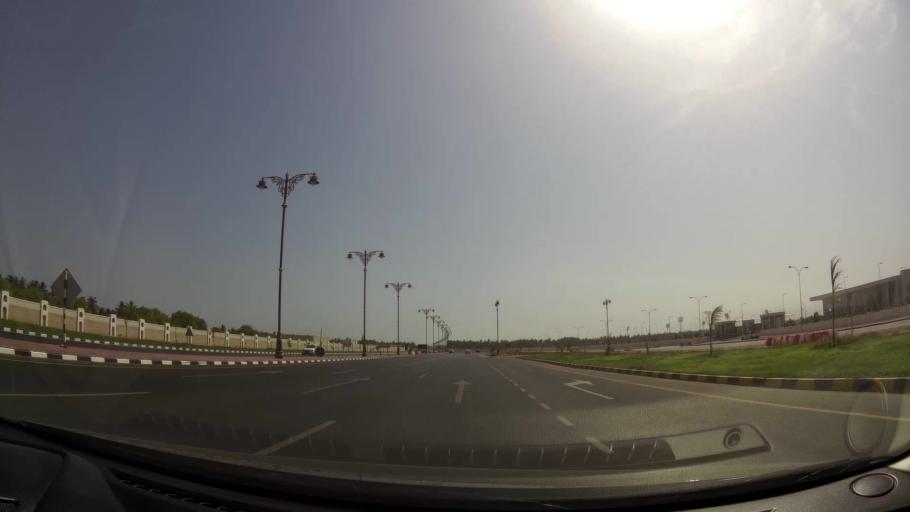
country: OM
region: Zufar
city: Salalah
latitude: 17.0282
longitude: 54.1309
